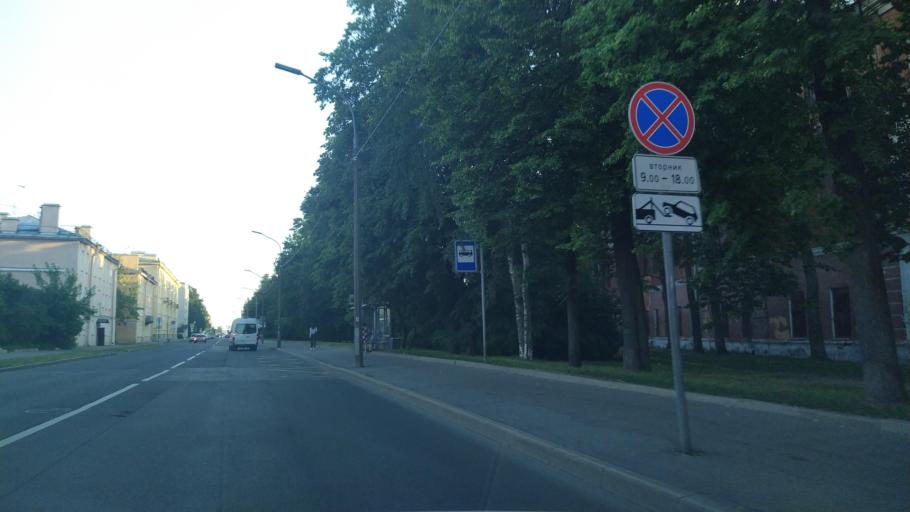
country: RU
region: St.-Petersburg
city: Kronshtadt
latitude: 60.0000
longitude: 29.7613
